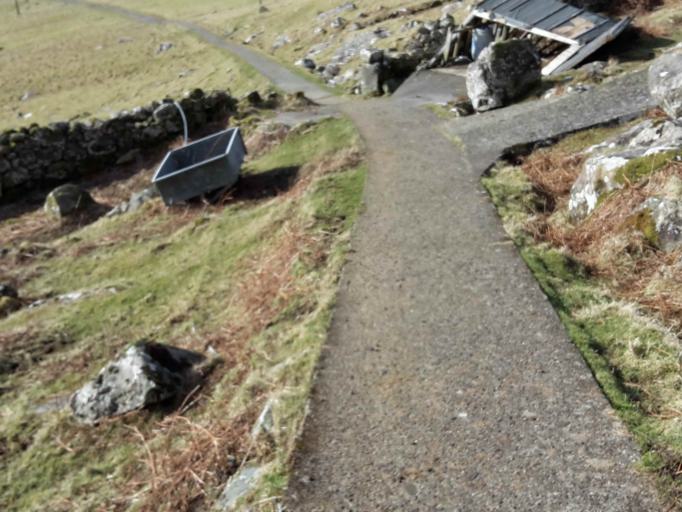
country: GB
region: Scotland
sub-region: Eilean Siar
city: Harris
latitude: 57.4294
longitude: -6.7811
